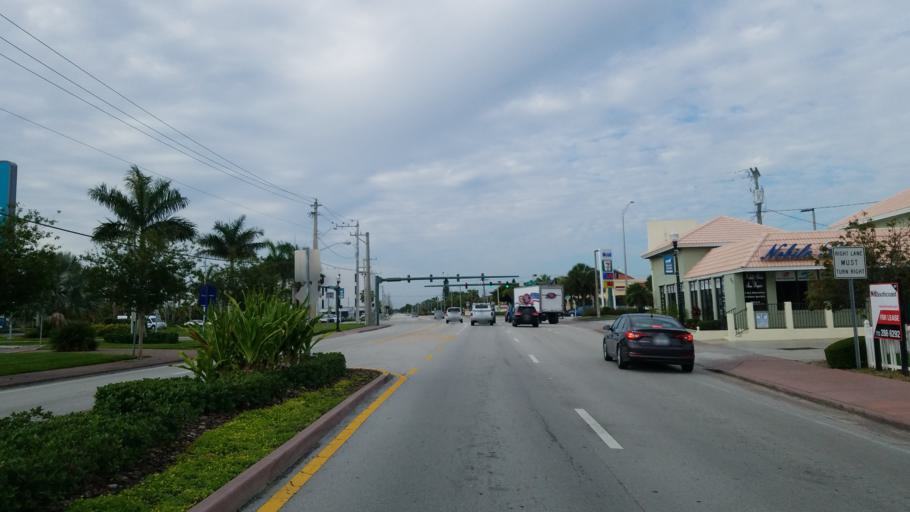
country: US
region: Florida
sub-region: Martin County
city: Stuart
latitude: 27.1922
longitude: -80.2529
